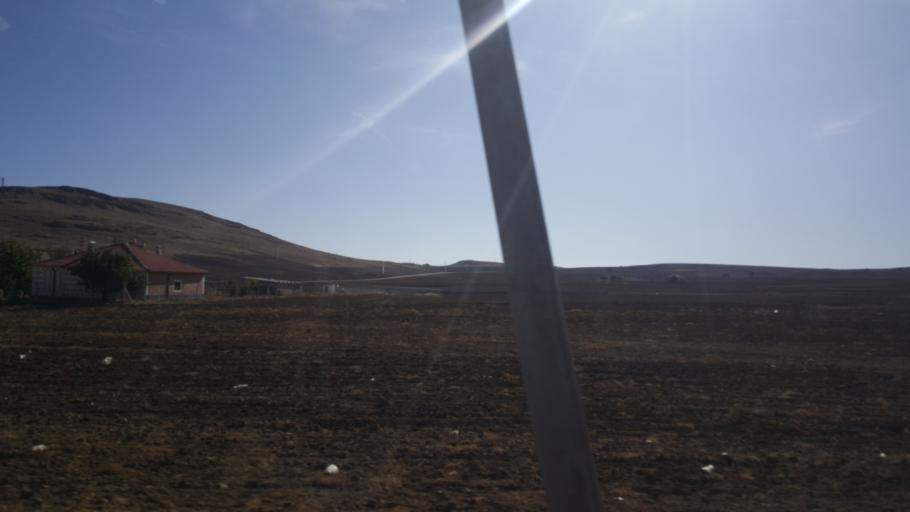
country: TR
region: Ankara
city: Yenice
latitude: 39.2736
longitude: 32.6674
